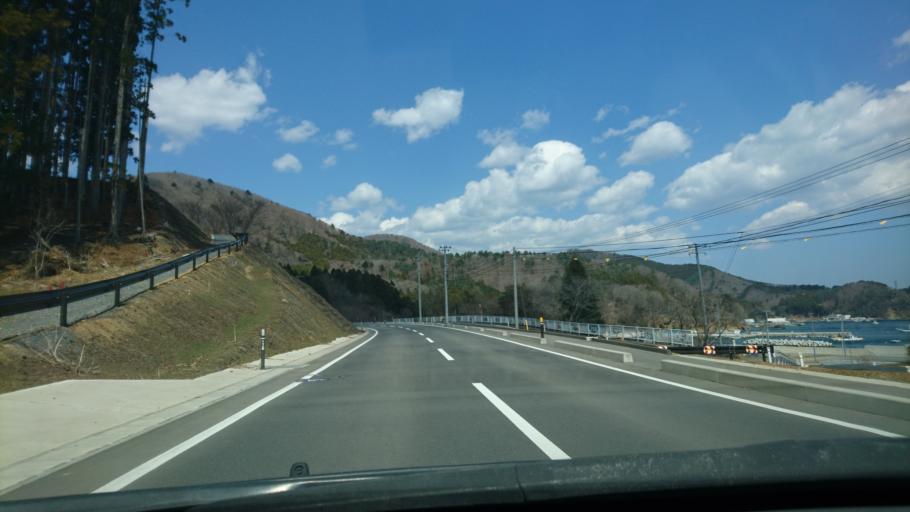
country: JP
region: Miyagi
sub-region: Oshika Gun
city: Onagawa Cho
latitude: 38.4653
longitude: 141.4734
